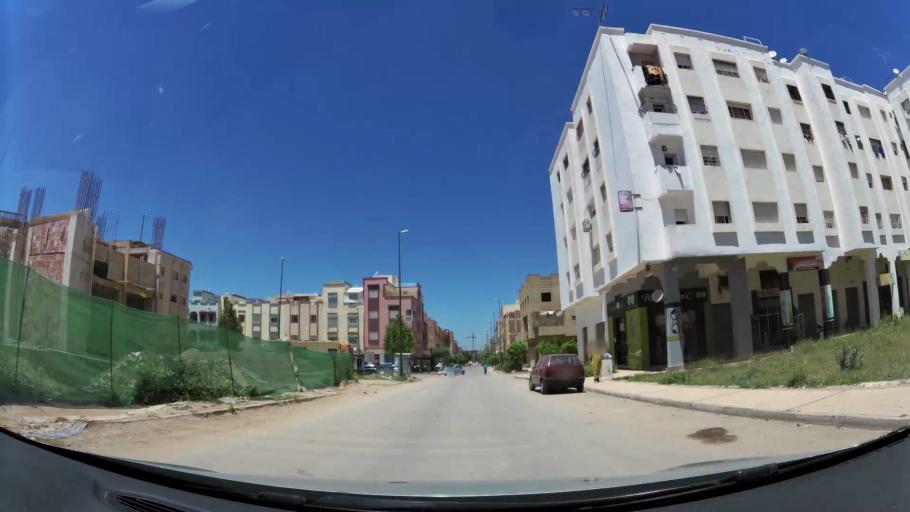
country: MA
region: Meknes-Tafilalet
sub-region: Meknes
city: Meknes
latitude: 33.8652
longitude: -5.5639
